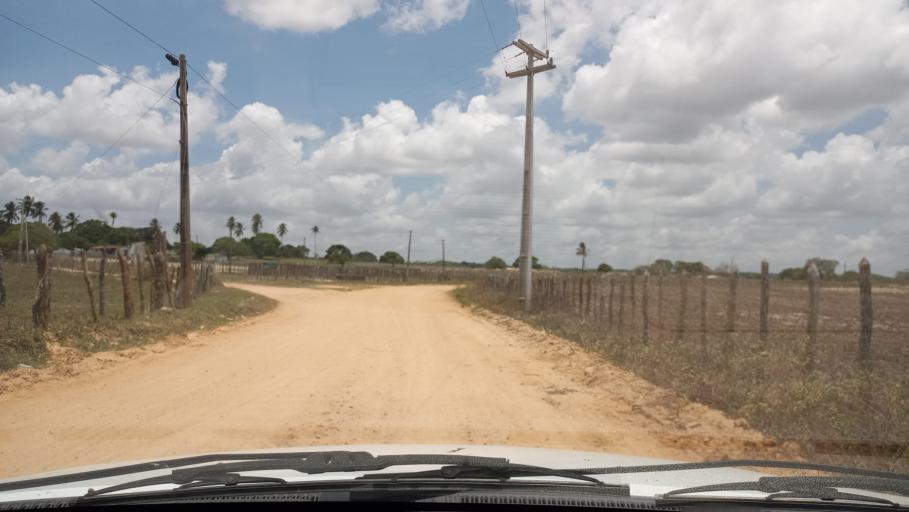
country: BR
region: Rio Grande do Norte
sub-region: Brejinho
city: Brejinho
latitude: -6.2842
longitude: -35.3435
